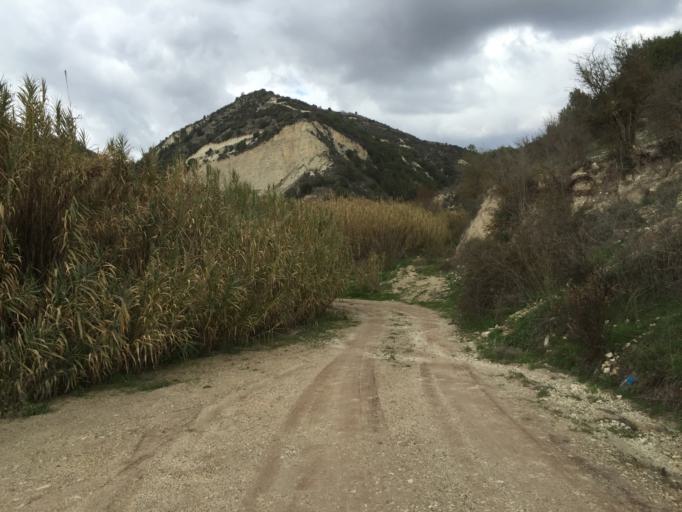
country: CY
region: Pafos
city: Mesogi
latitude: 34.8229
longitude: 32.5220
